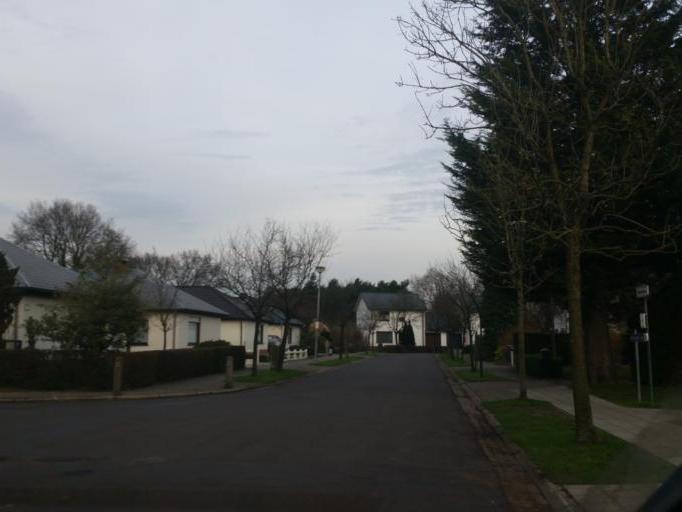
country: BE
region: Flanders
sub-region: Provincie Antwerpen
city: Sint-Katelijne-Waver
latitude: 51.0663
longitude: 4.5255
